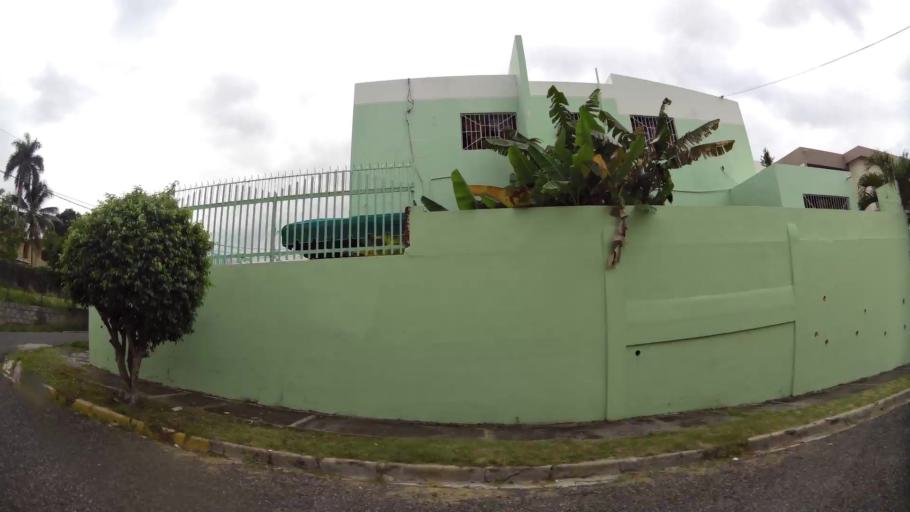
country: DO
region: Nacional
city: La Agustina
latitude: 18.4953
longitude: -69.9339
